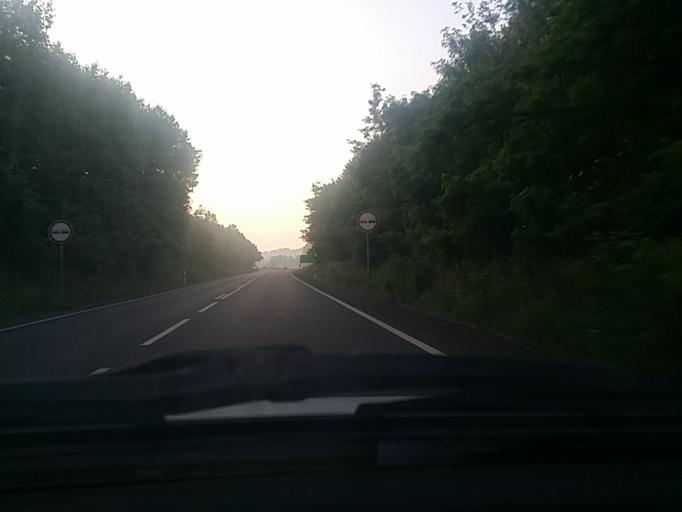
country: HU
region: Pest
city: Gyomro
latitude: 47.4306
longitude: 19.4202
